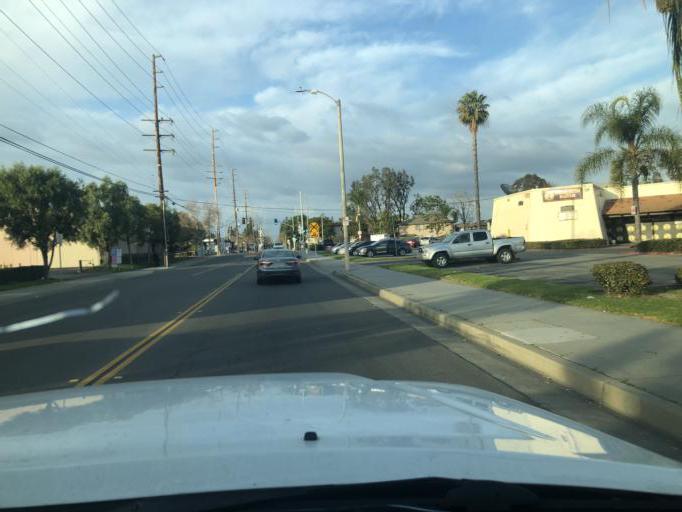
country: US
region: California
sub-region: Orange County
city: Tustin
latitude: 33.7341
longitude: -117.8449
